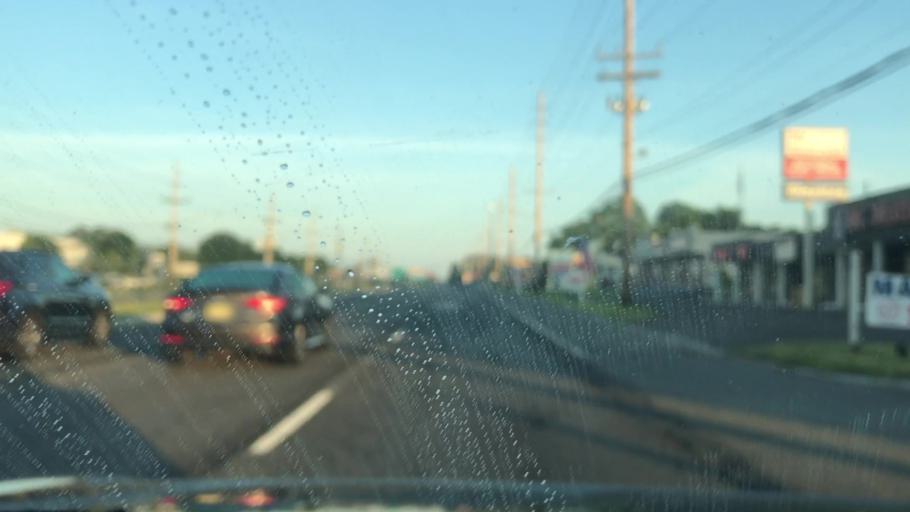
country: US
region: New Jersey
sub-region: Ocean County
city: Toms River
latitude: 39.9637
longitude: -74.1901
